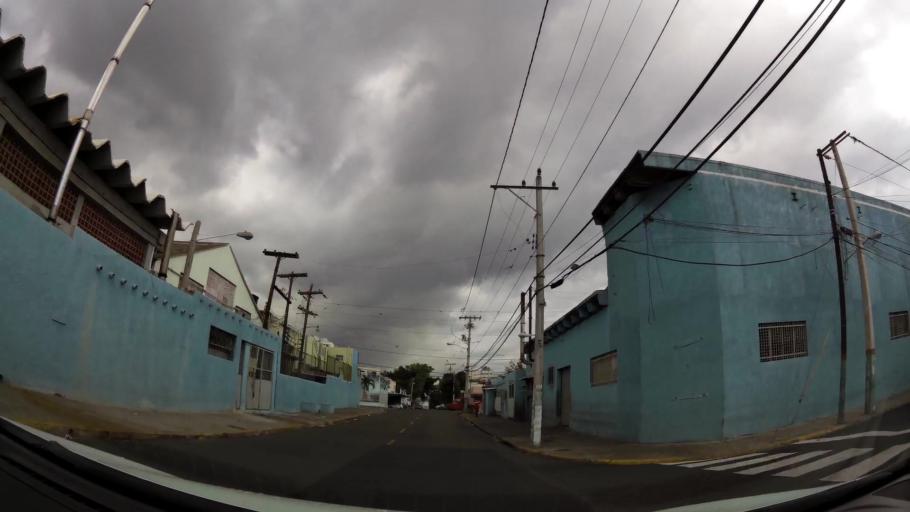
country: DO
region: Nacional
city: La Agustina
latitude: 18.4929
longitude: -69.9199
